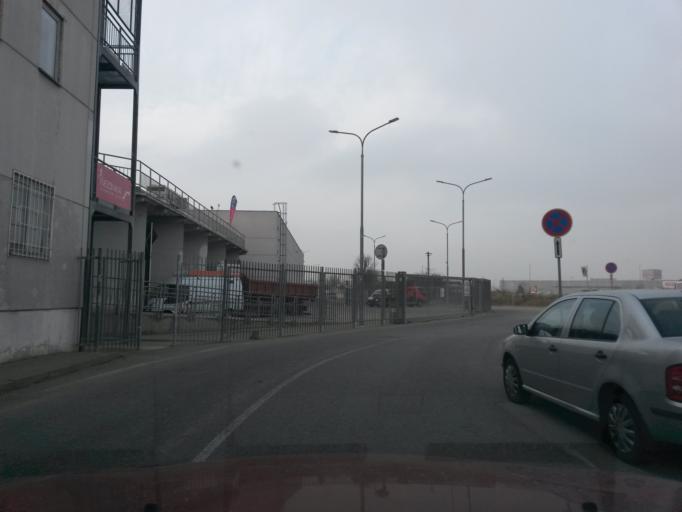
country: SK
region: Kosicky
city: Kosice
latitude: 48.6957
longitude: 21.2396
